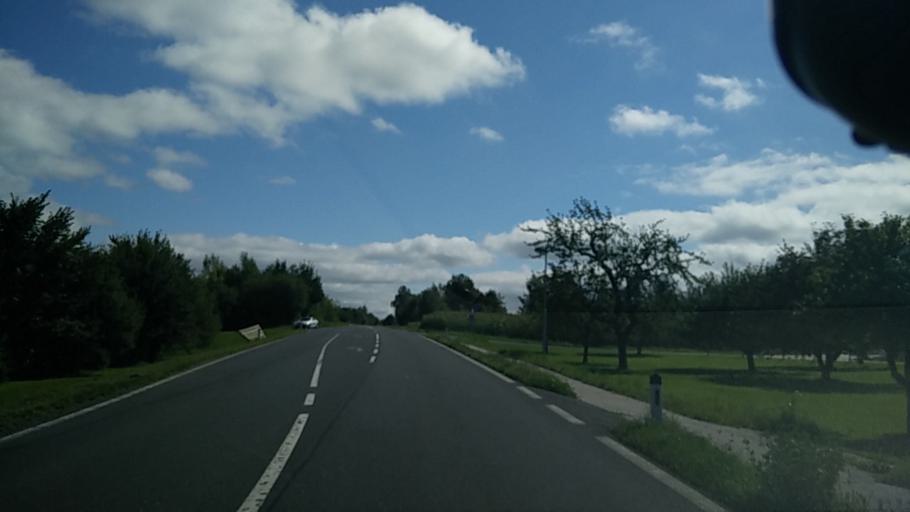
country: AT
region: Carinthia
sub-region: Politischer Bezirk Villach Land
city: Finkenstein am Faaker See
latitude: 46.5609
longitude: 13.8530
